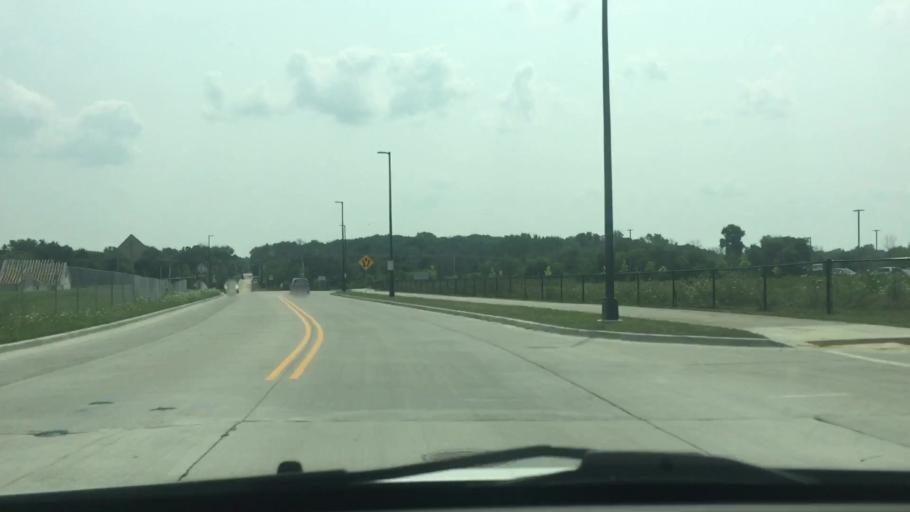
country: US
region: Wisconsin
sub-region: Milwaukee County
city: Greendale
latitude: 42.9042
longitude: -87.9413
